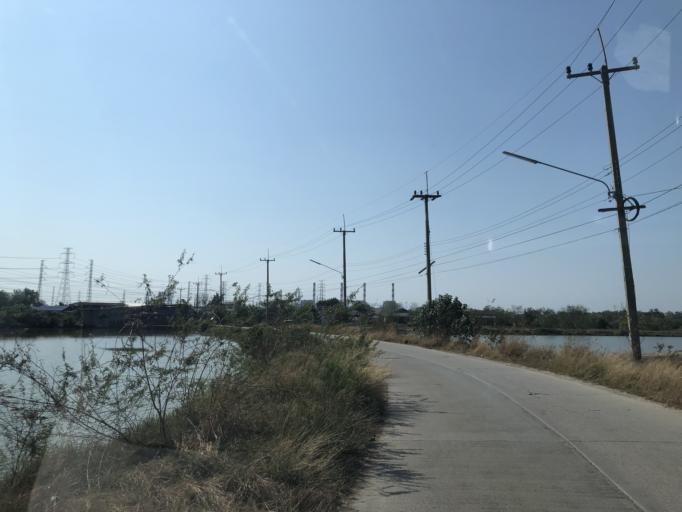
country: TH
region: Chachoengsao
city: Bang Pakong
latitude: 13.5185
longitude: 101.0218
